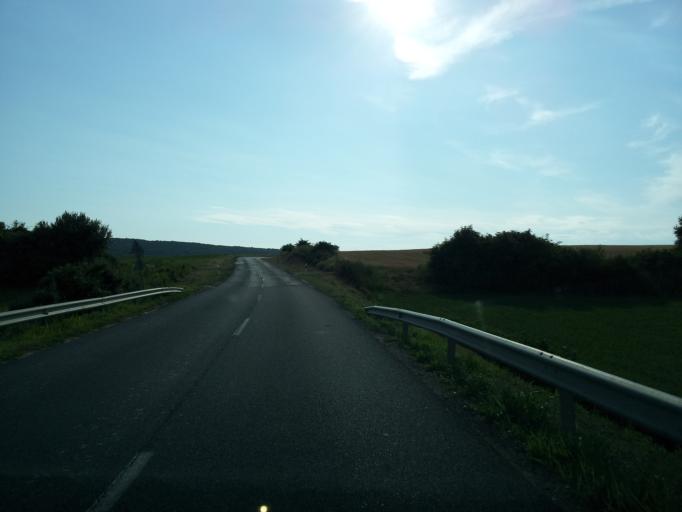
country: HU
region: Veszprem
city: Urkut
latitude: 46.9912
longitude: 17.6757
